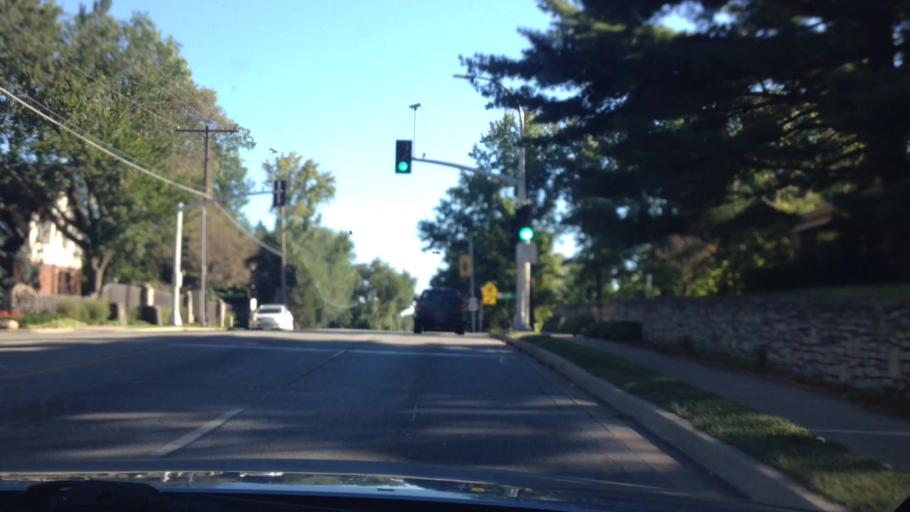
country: US
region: Kansas
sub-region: Johnson County
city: Westwood
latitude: 39.0380
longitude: -94.6120
